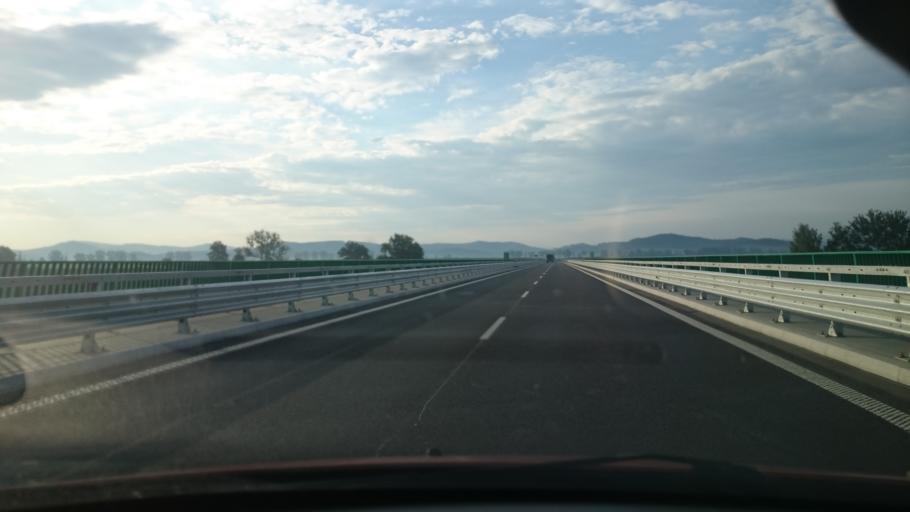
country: PL
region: Lower Silesian Voivodeship
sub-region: Powiat klodzki
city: Klodzko
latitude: 50.4035
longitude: 16.6431
